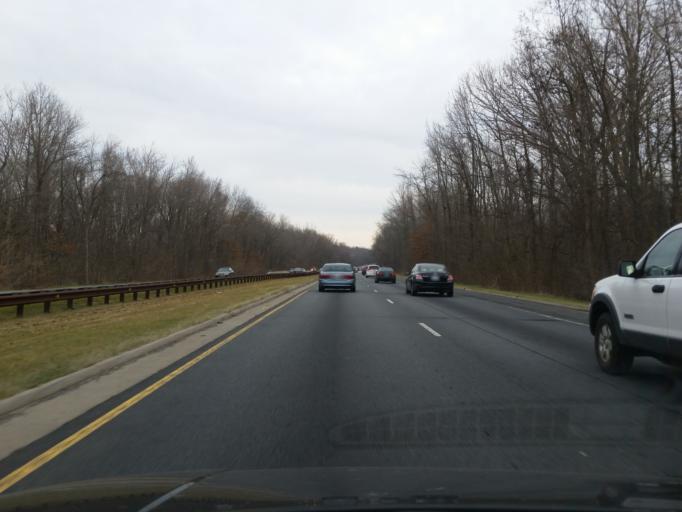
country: US
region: Maryland
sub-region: Prince George's County
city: South Laurel
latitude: 39.0667
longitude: -76.8332
